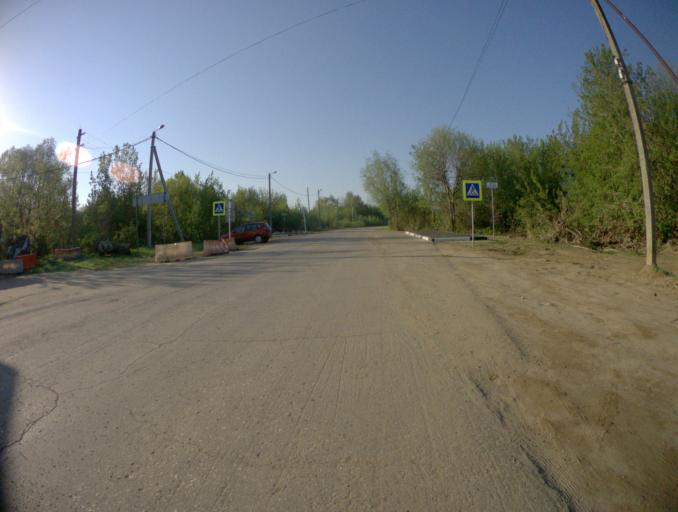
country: RU
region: Vladimir
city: Vyazniki
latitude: 56.2545
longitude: 42.1788
